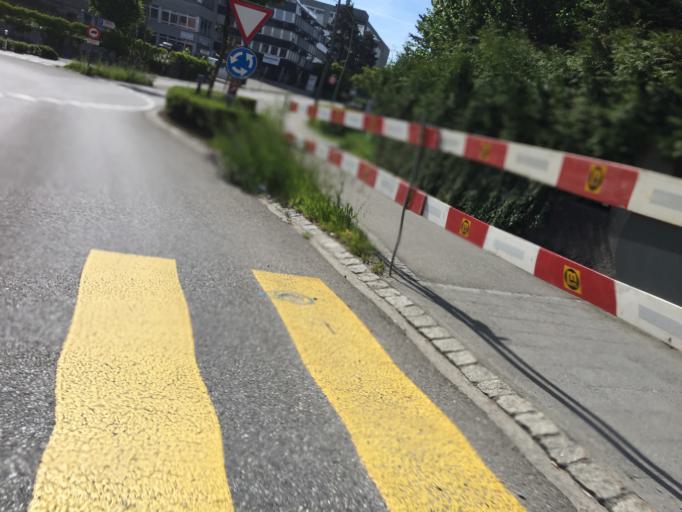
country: CH
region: Bern
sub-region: Bern-Mittelland District
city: Muri
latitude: 46.9323
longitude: 7.5079
